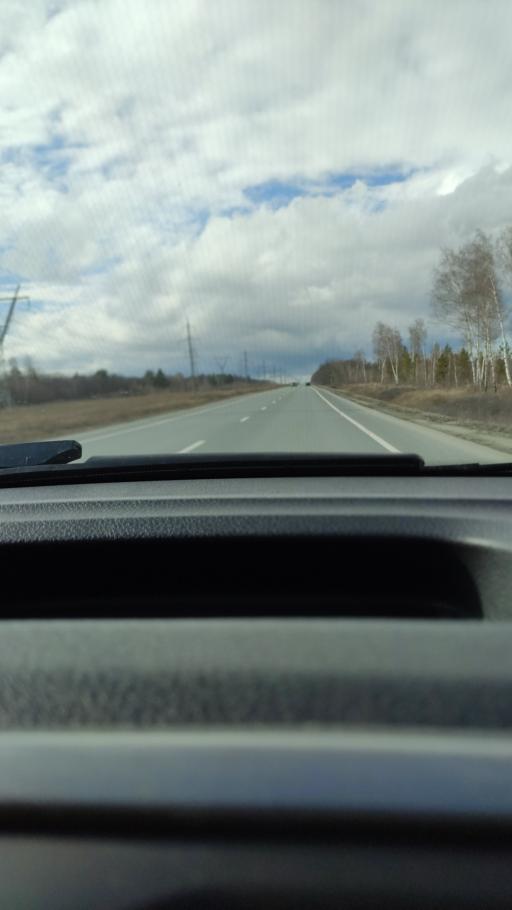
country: RU
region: Samara
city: Bogatyr'
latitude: 53.4939
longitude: 49.9672
